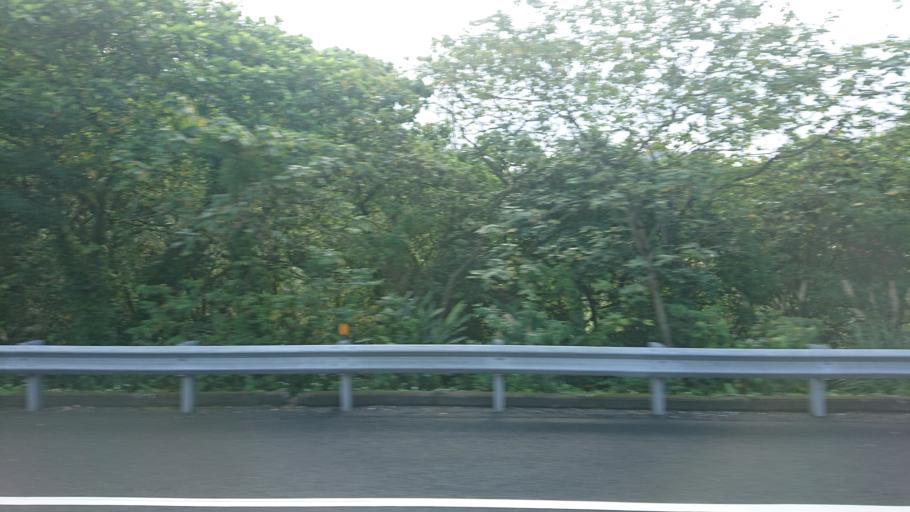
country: TW
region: Taipei
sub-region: Taipei
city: Banqiao
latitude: 24.9832
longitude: 121.4728
